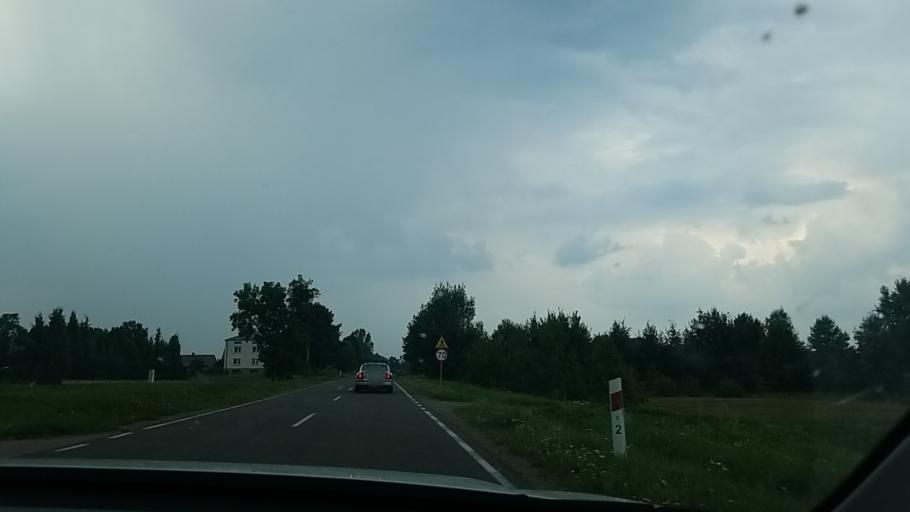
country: PL
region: Lublin Voivodeship
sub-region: Powiat leczynski
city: Cycow
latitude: 51.2707
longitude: 23.0960
